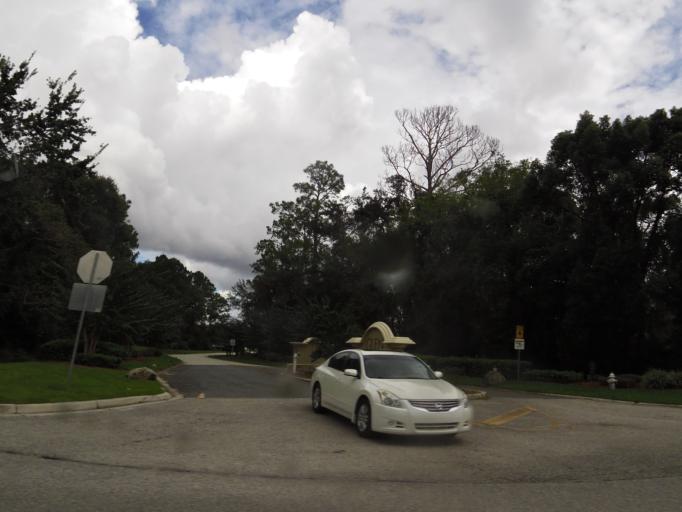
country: US
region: Florida
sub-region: Clay County
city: Lakeside
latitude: 30.1036
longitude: -81.7891
